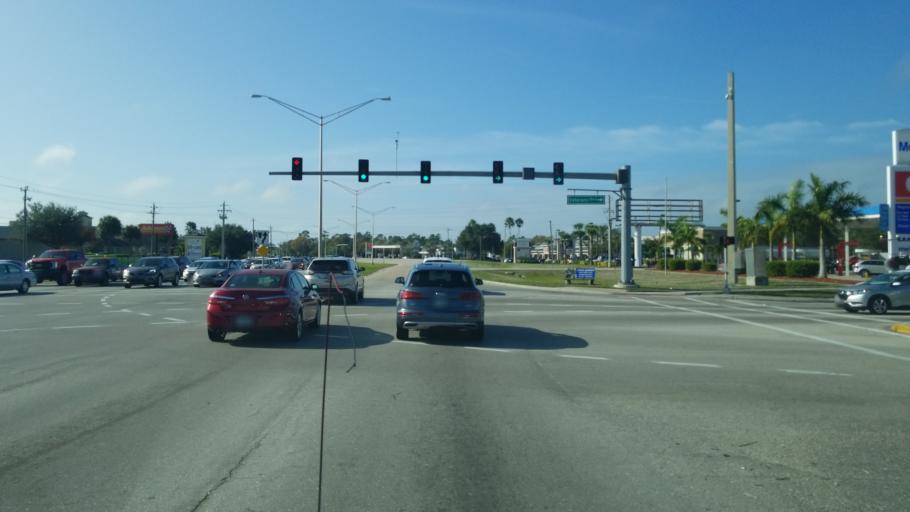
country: US
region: Florida
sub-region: Charlotte County
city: Harbour Heights
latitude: 27.0170
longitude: -82.0515
